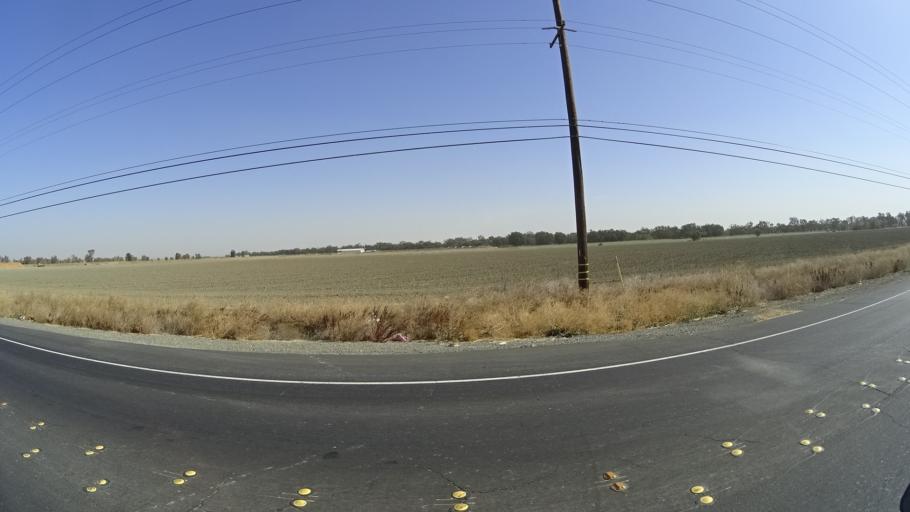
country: US
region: California
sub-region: Yolo County
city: Woodland
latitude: 38.6382
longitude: -121.7293
